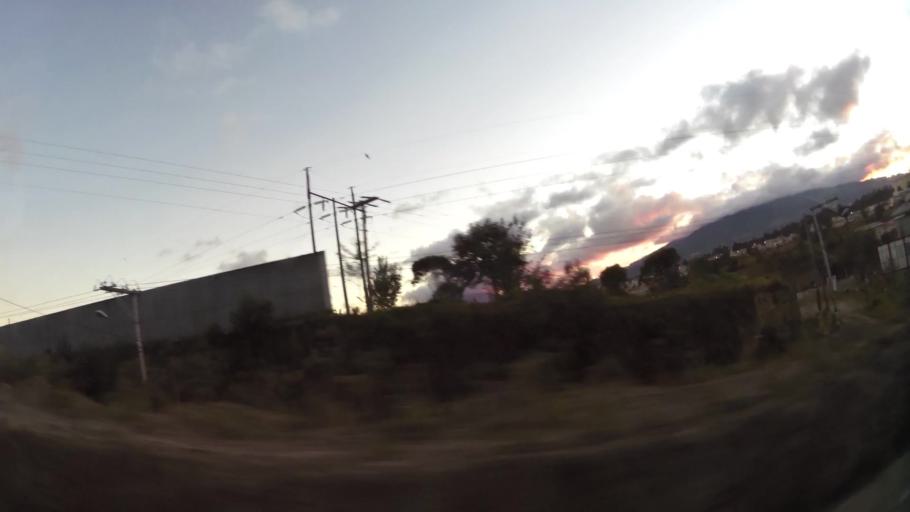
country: GT
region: Quetzaltenango
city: Olintepeque
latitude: 14.8635
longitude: -91.5336
